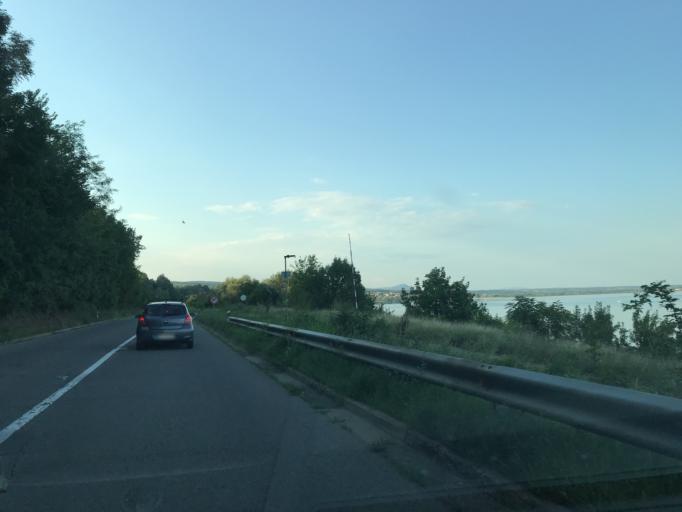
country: RO
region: Mehedinti
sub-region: Comuna Gogosu
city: Ostrovu Mare
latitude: 44.4659
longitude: 22.4503
